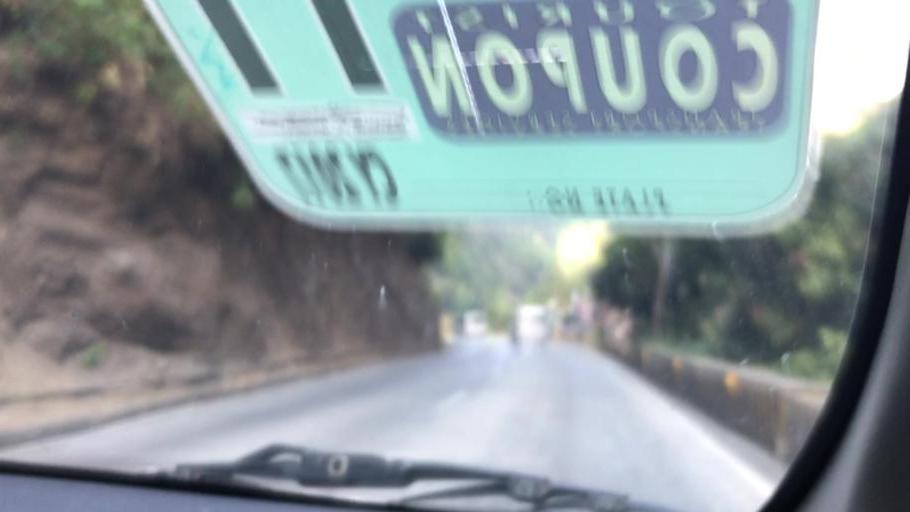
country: PH
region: Cordillera
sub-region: Province of Benguet
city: Tuba
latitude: 16.3248
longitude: 120.6144
